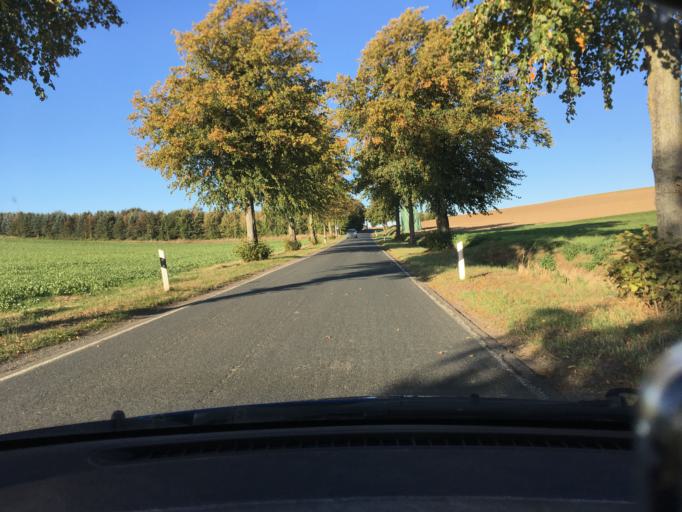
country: DE
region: Lower Saxony
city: Bad Munder am Deister
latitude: 52.2143
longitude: 9.4426
